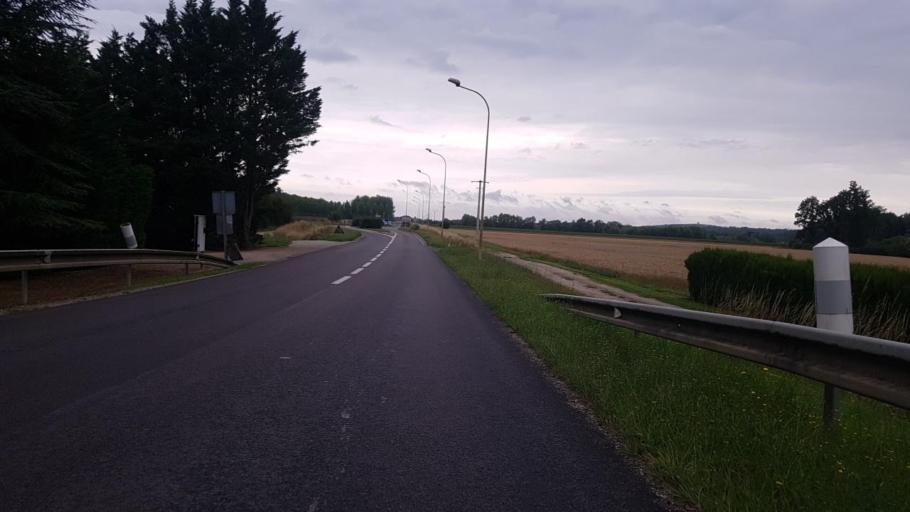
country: FR
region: Champagne-Ardenne
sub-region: Departement de la Marne
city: Vitry-le-Francois
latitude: 48.7467
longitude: 4.6966
